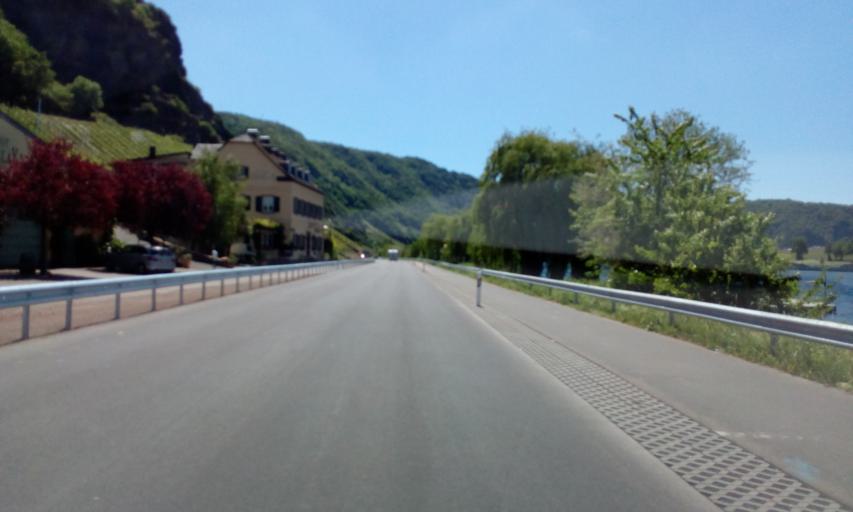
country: DE
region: Rheinland-Pfalz
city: Wintrich
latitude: 49.8752
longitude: 6.9497
